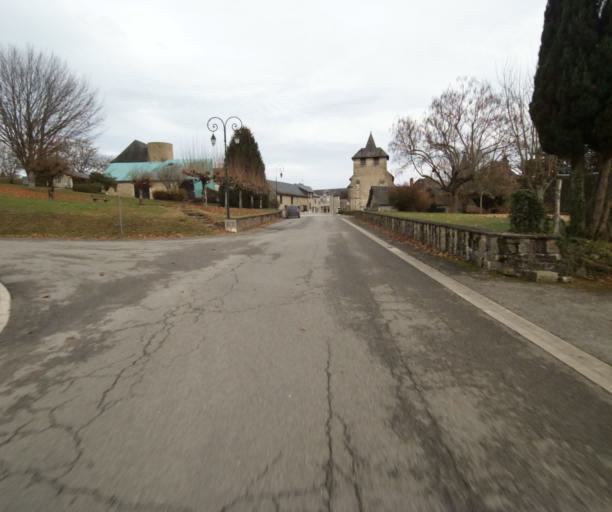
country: FR
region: Limousin
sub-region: Departement de la Correze
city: Chameyrat
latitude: 45.2339
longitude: 1.6965
